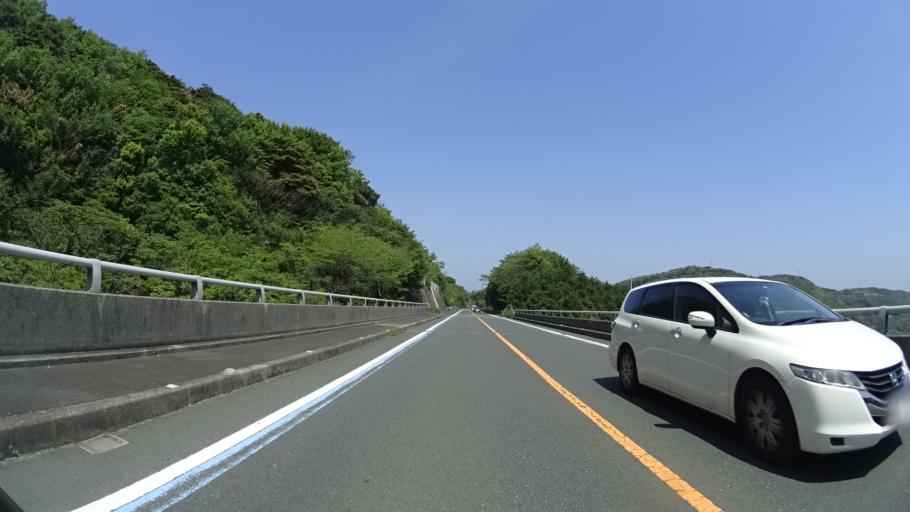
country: JP
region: Ehime
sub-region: Nishiuwa-gun
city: Ikata-cho
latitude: 33.4606
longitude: 132.2732
